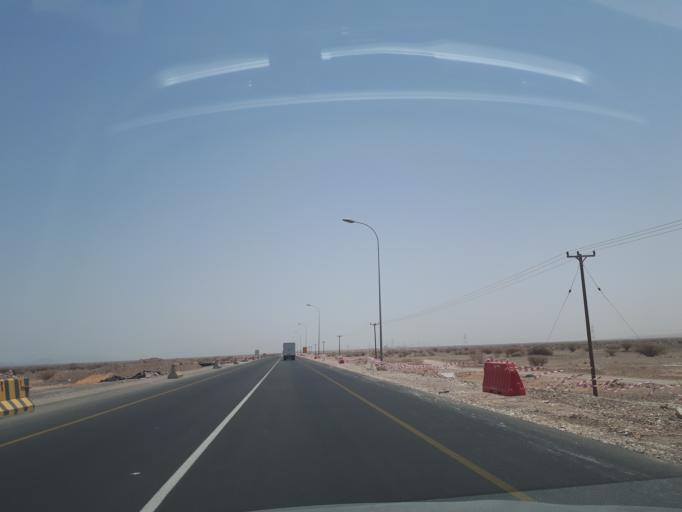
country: OM
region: Ash Sharqiyah
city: Badiyah
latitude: 22.4258
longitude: 59.0400
